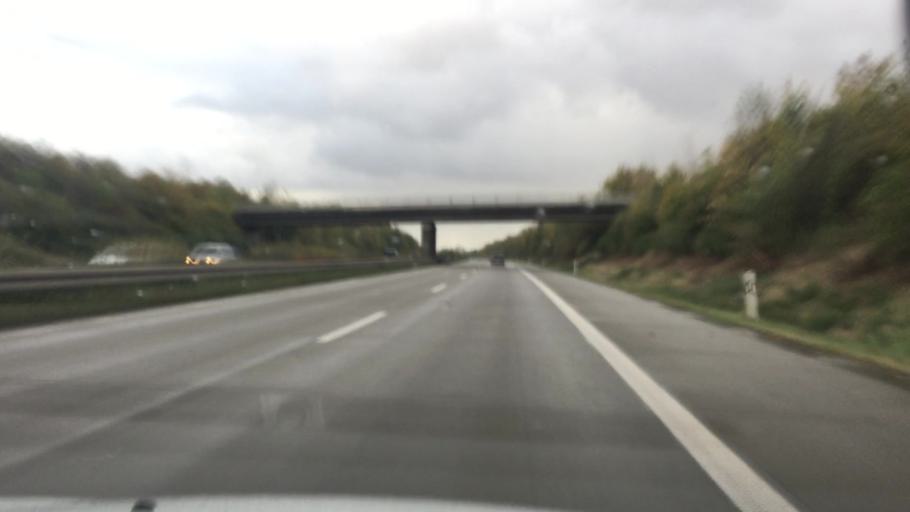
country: DE
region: Saxony-Anhalt
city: Hohendodeleben
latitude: 52.1036
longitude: 11.5284
